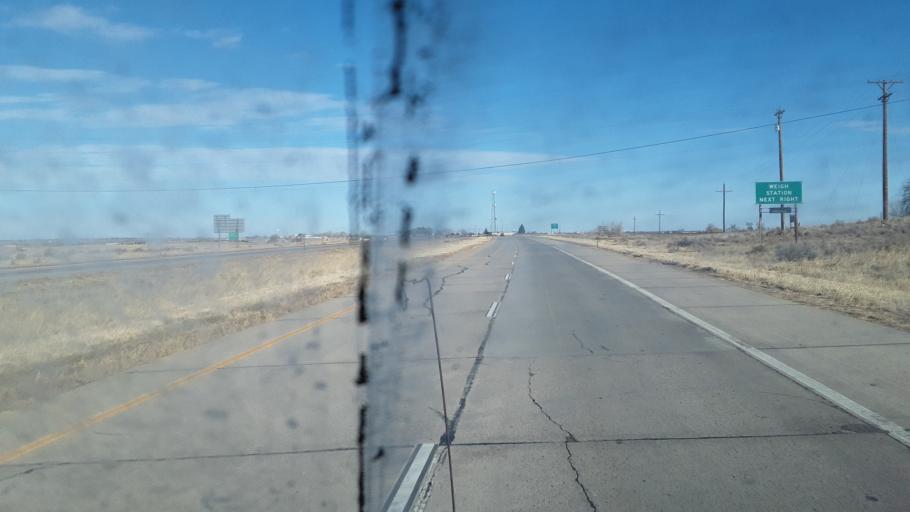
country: US
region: Colorado
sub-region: Morgan County
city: Fort Morgan
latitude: 40.2433
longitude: -103.9064
